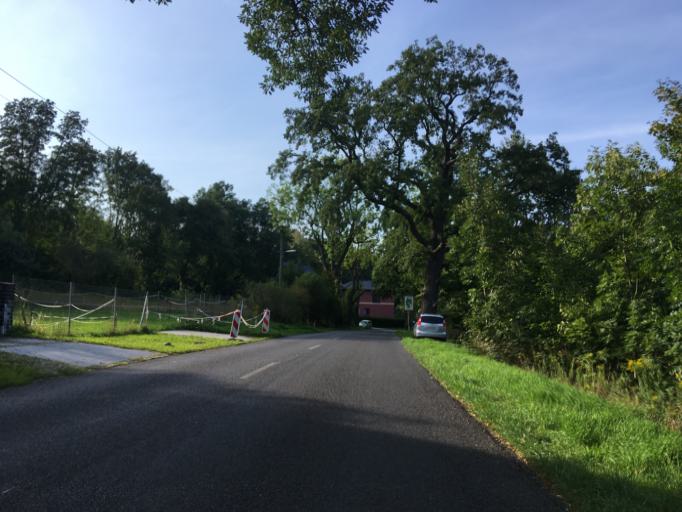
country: DE
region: Brandenburg
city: Frankfurt (Oder)
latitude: 52.3068
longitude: 14.5591
